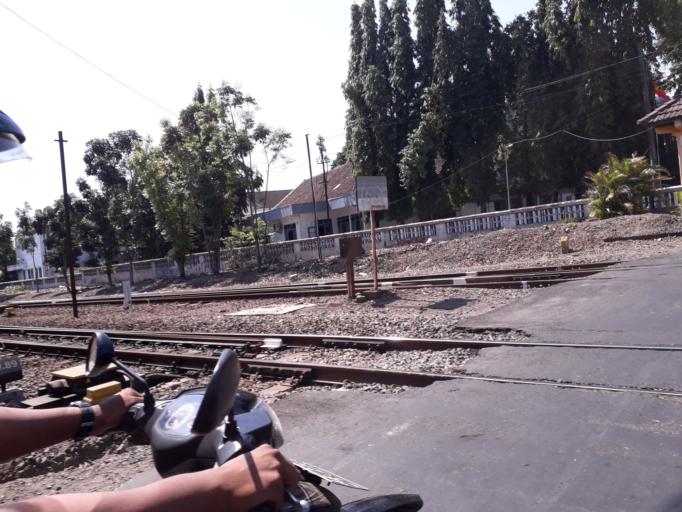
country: ID
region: Daerah Istimewa Yogyakarta
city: Yogyakarta
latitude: -7.7904
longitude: 110.3730
